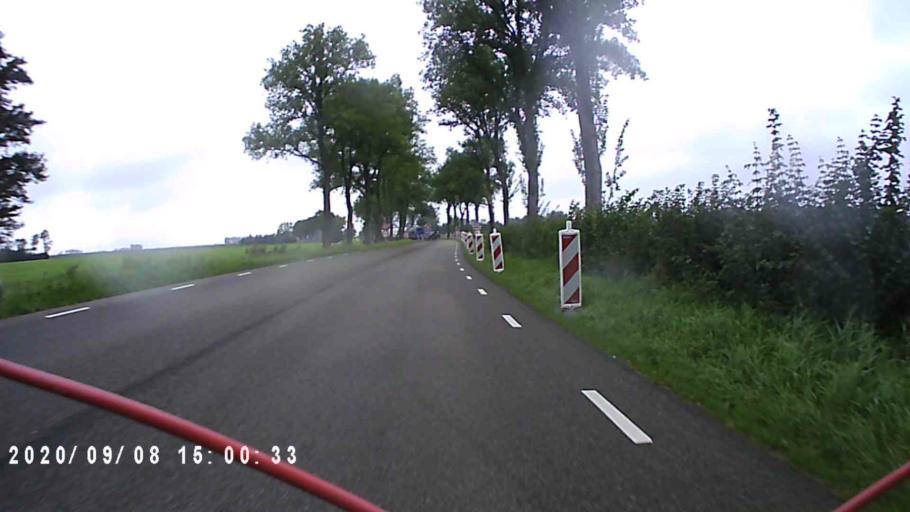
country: NL
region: Groningen
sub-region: Gemeente Slochteren
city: Slochteren
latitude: 53.2718
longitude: 6.7636
